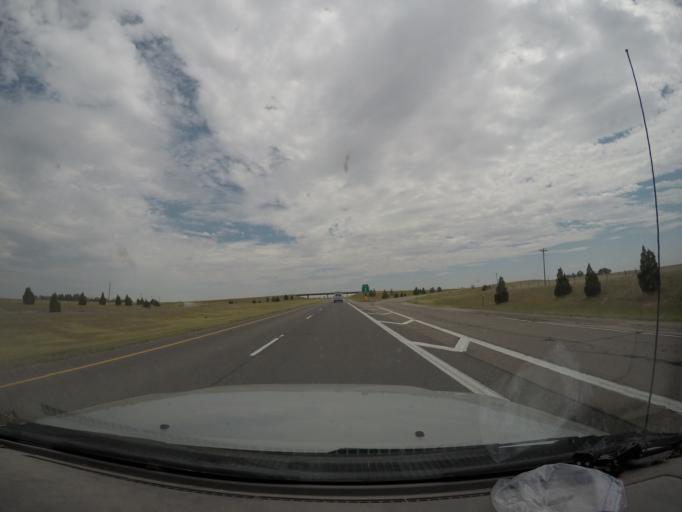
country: US
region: Wyoming
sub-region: Laramie County
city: Pine Bluffs
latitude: 41.1918
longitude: -103.8979
